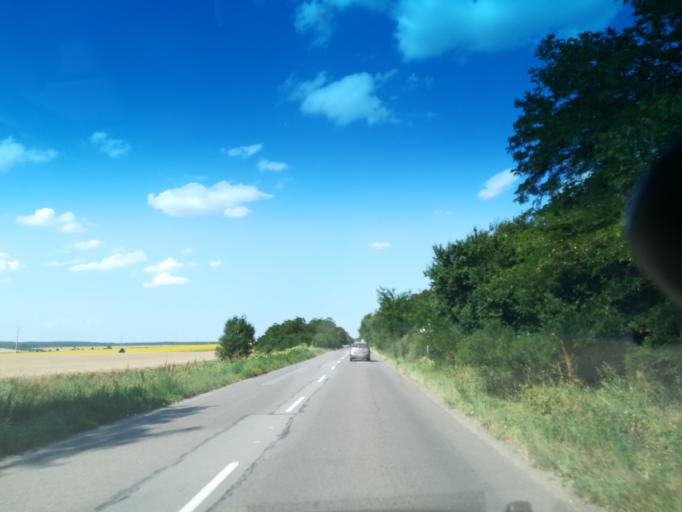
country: BG
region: Stara Zagora
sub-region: Obshtina Chirpan
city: Chirpan
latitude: 42.2393
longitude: 25.4013
